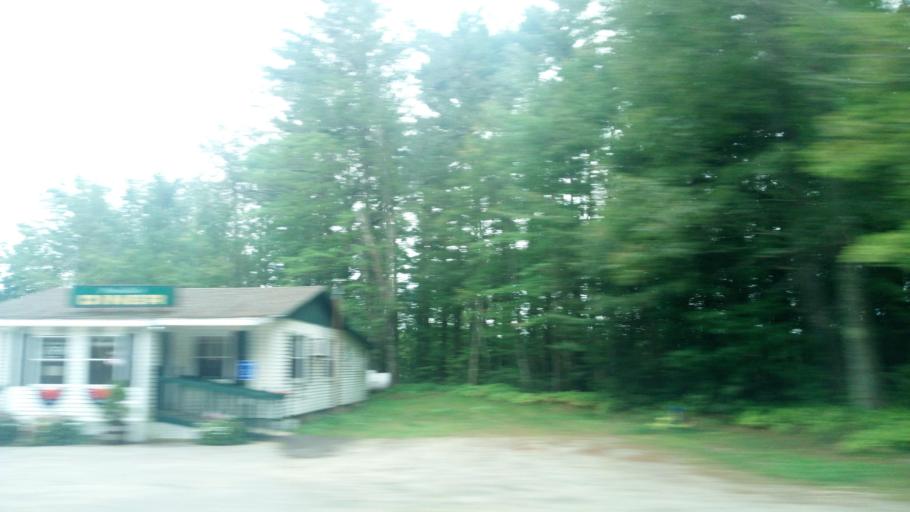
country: US
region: Maine
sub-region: Kennebec County
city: Windsor
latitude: 44.2791
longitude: -69.6029
